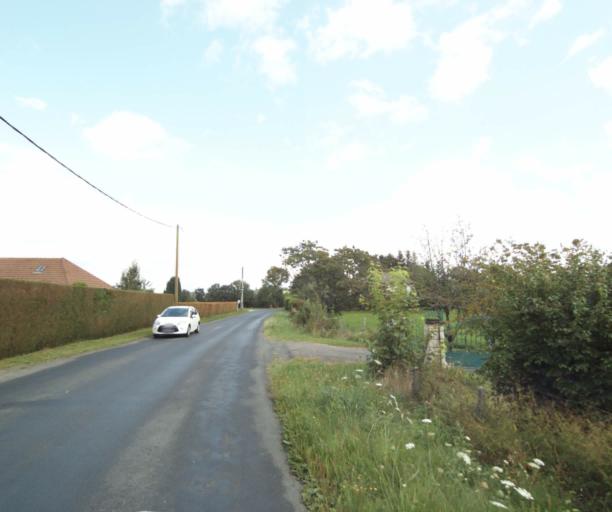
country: FR
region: Limousin
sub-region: Departement de la Correze
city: Sainte-Fortunade
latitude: 45.1980
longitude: 1.8202
